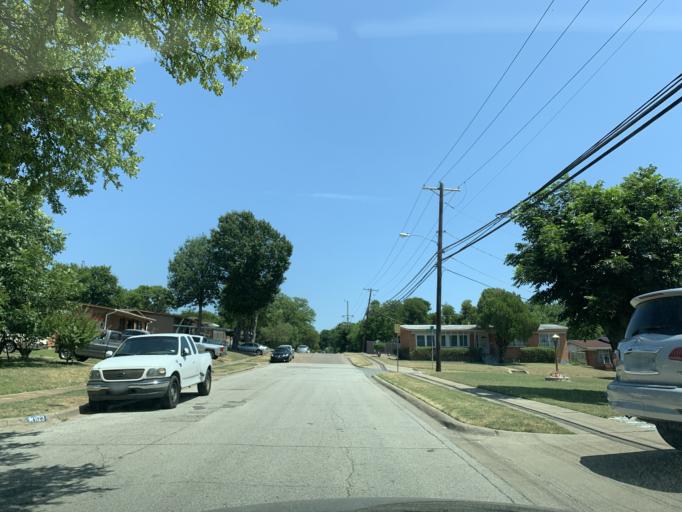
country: US
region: Texas
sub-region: Dallas County
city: Cockrell Hill
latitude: 32.6913
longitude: -96.8094
